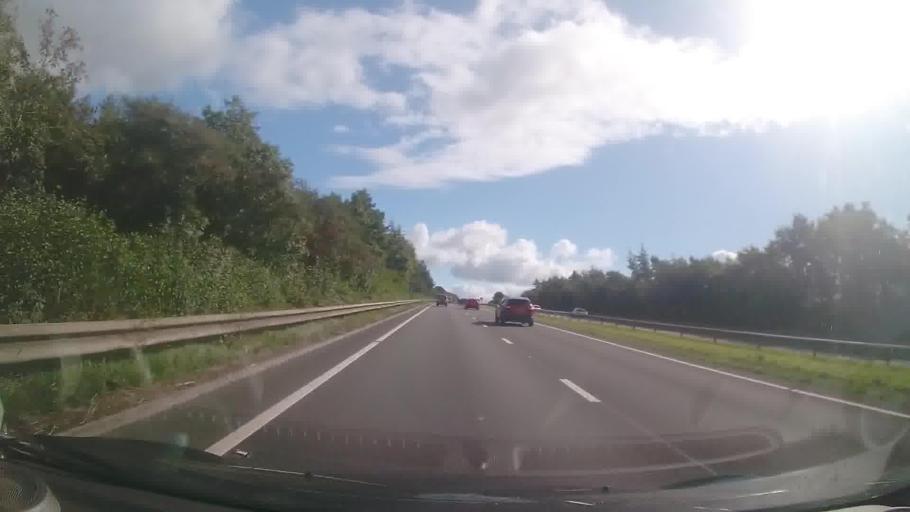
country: GB
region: Wales
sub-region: Carmarthenshire
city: Llanddarog
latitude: 51.8405
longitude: -4.2389
